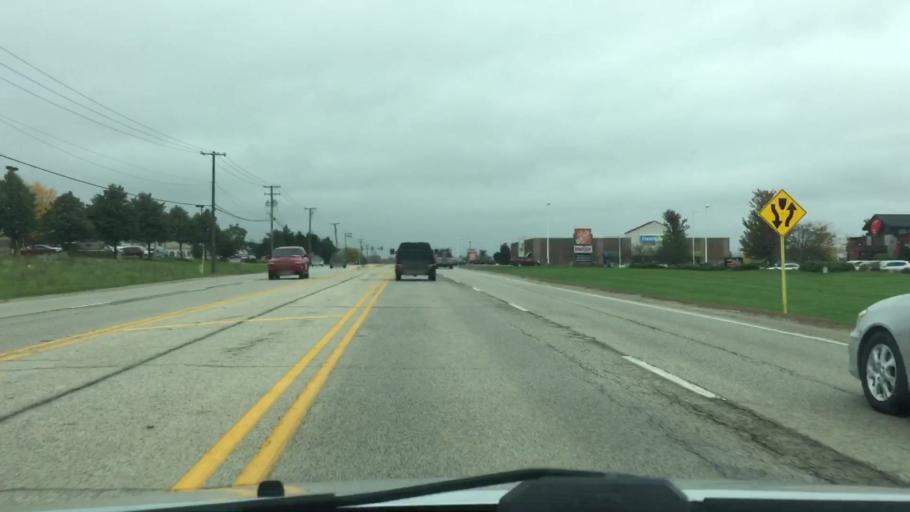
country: US
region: Illinois
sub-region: McHenry County
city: McCullom Lake
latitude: 42.3619
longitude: -88.2673
